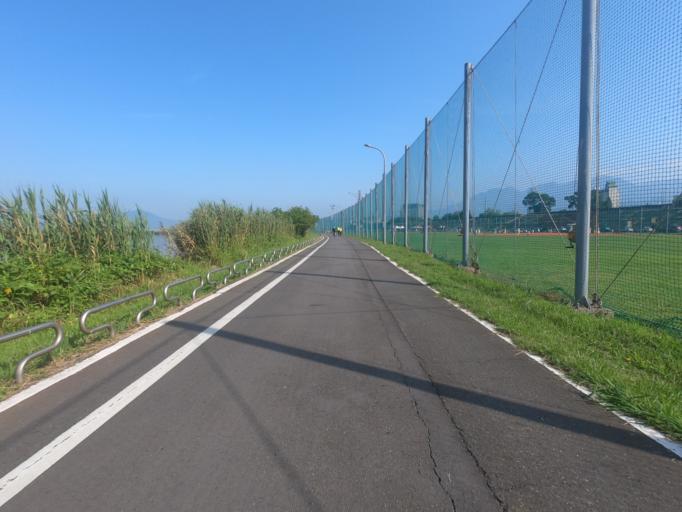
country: TW
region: Taipei
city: Taipei
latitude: 25.0927
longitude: 121.5131
